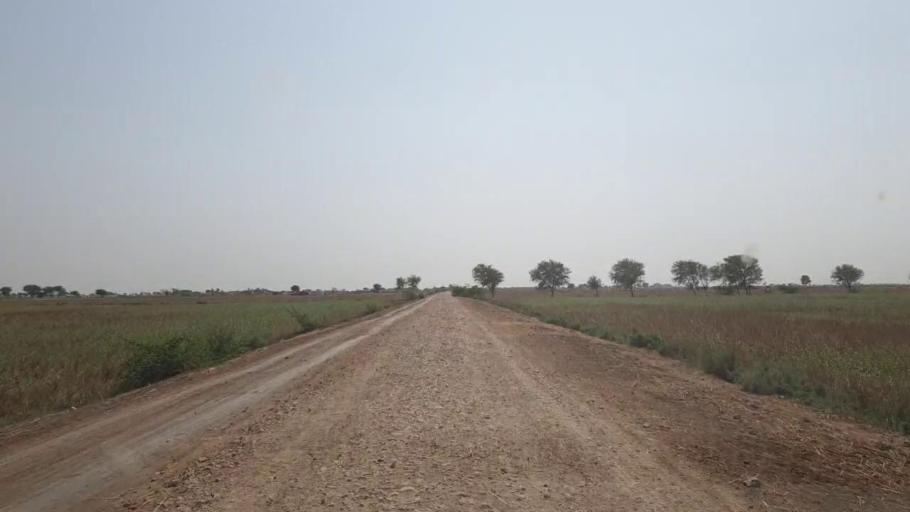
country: PK
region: Sindh
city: Jati
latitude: 24.4350
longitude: 68.5523
